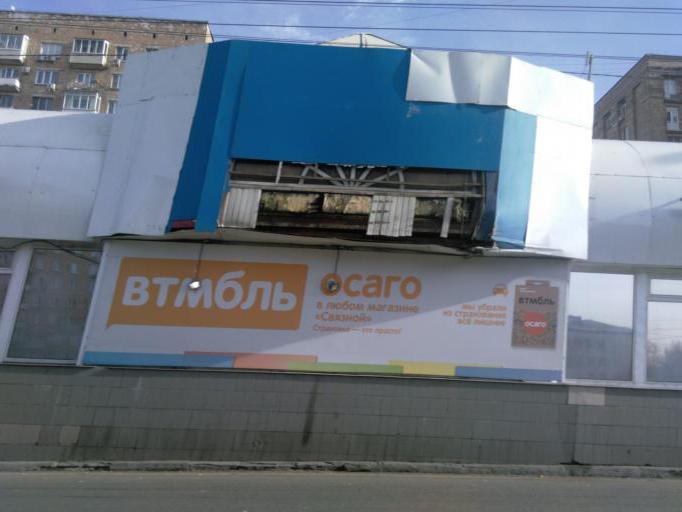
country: RU
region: Moscow
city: Mar'ina Roshcha
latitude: 55.8079
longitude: 37.6374
